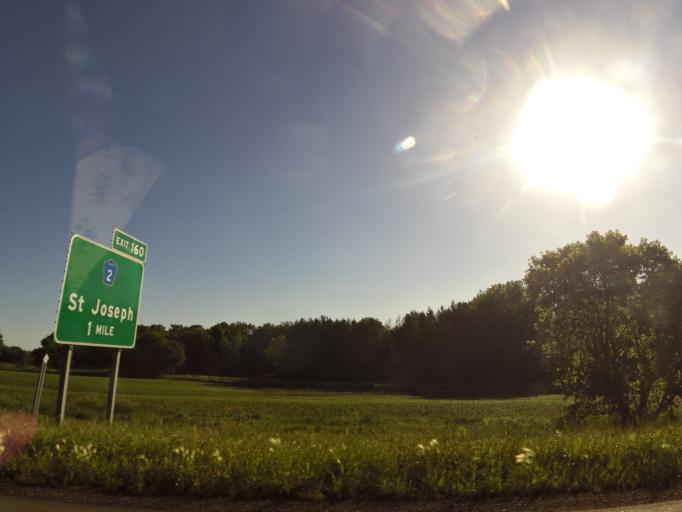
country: US
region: Minnesota
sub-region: Stearns County
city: Saint Joseph
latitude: 45.5448
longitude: -94.3230
